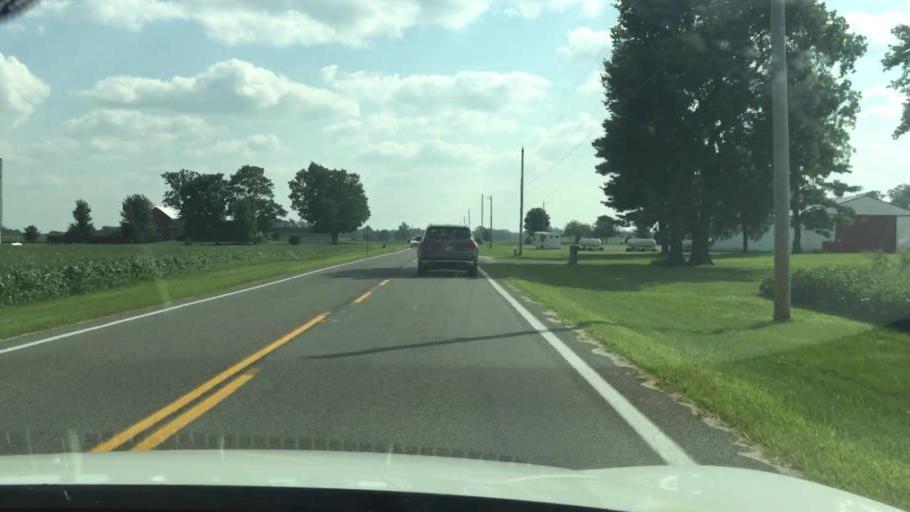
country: US
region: Ohio
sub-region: Champaign County
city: North Lewisburg
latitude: 40.1877
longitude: -83.5186
